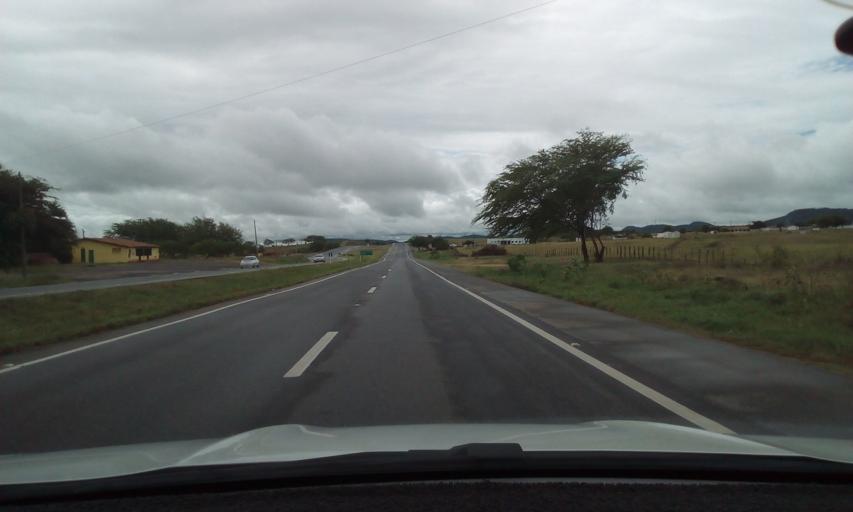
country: BR
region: Paraiba
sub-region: Mogeiro
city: Mogeiro
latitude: -7.2018
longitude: -35.4967
